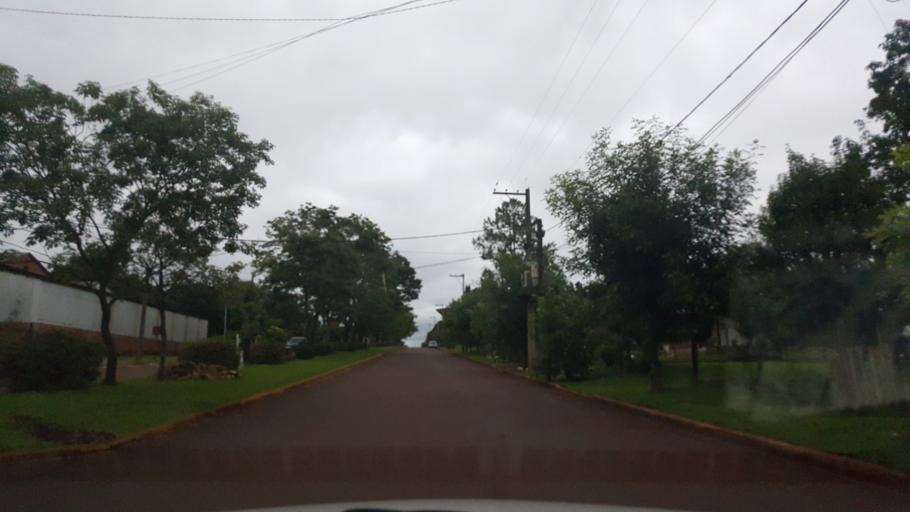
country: AR
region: Misiones
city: Ruiz de Montoya
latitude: -26.9686
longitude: -55.0582
